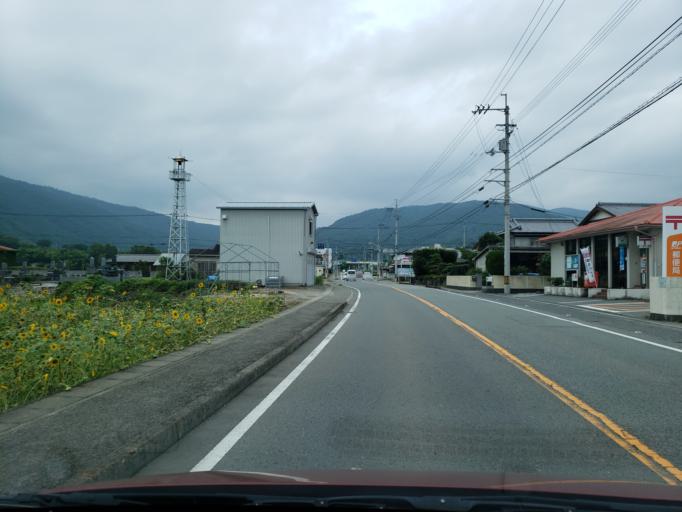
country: JP
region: Tokushima
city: Kamojimacho-jogejima
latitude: 34.1171
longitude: 134.3531
